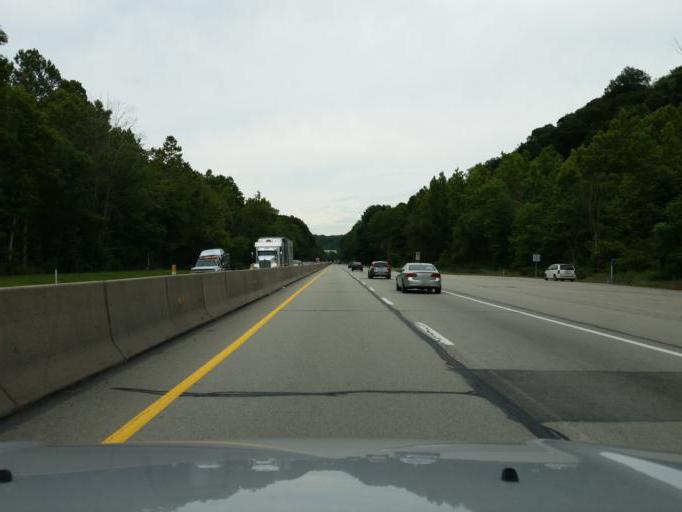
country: US
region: Pennsylvania
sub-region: Westmoreland County
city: Level Green
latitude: 40.4033
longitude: -79.7074
